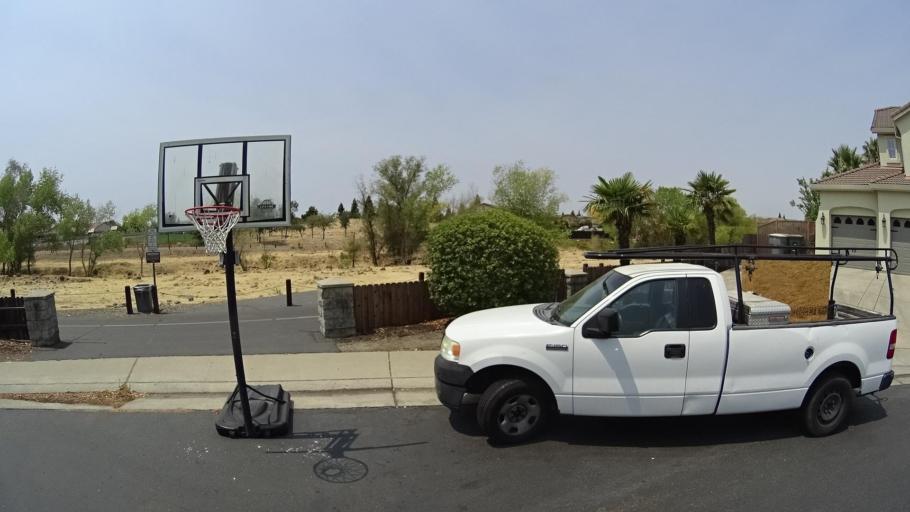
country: US
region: California
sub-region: Placer County
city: Rocklin
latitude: 38.8008
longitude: -121.2796
